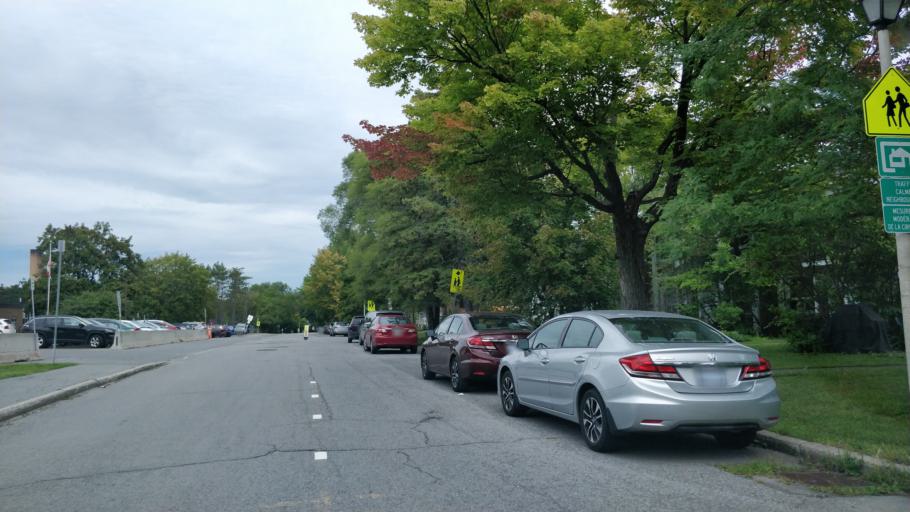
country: CA
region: Quebec
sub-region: Outaouais
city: Gatineau
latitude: 45.4497
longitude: -75.6551
